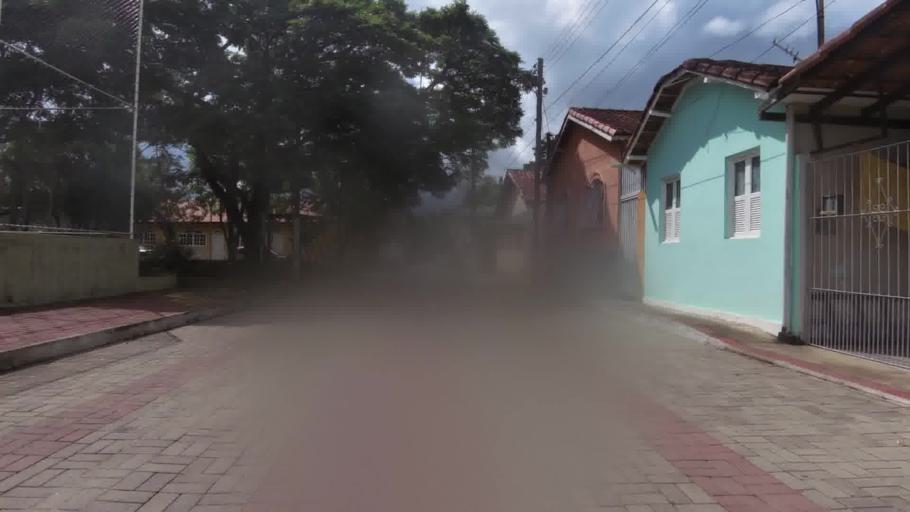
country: BR
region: Espirito Santo
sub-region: Piuma
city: Piuma
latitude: -20.8033
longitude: -40.6550
